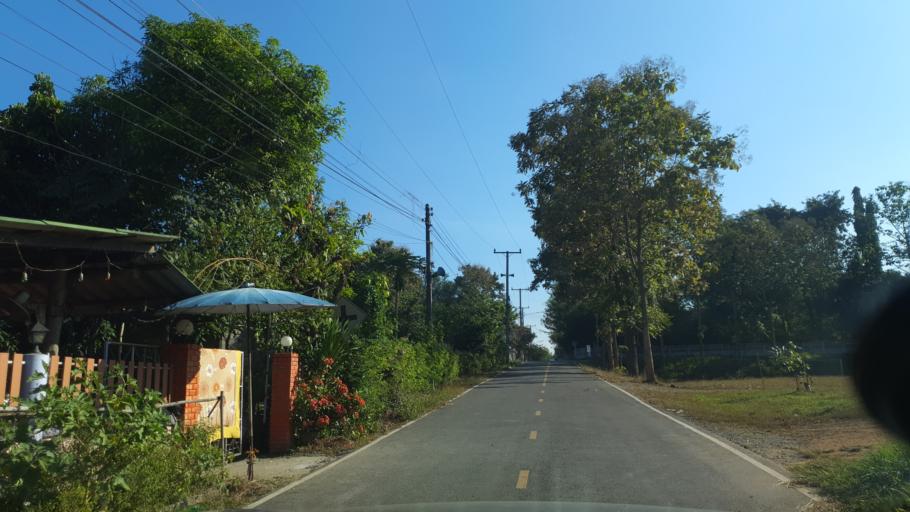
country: TH
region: Chiang Mai
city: Mae On
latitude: 18.7479
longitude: 99.2195
